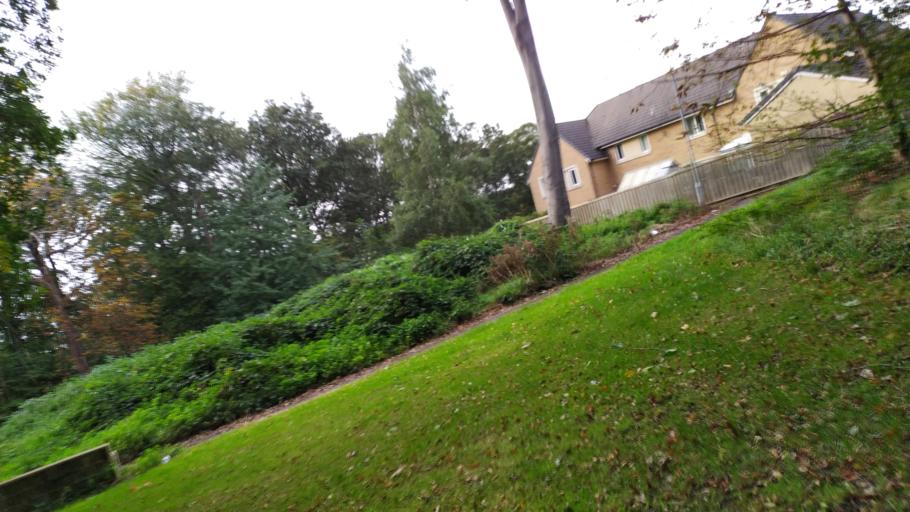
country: GB
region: England
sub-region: City and Borough of Leeds
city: Leeds
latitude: 53.8201
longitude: -1.5913
